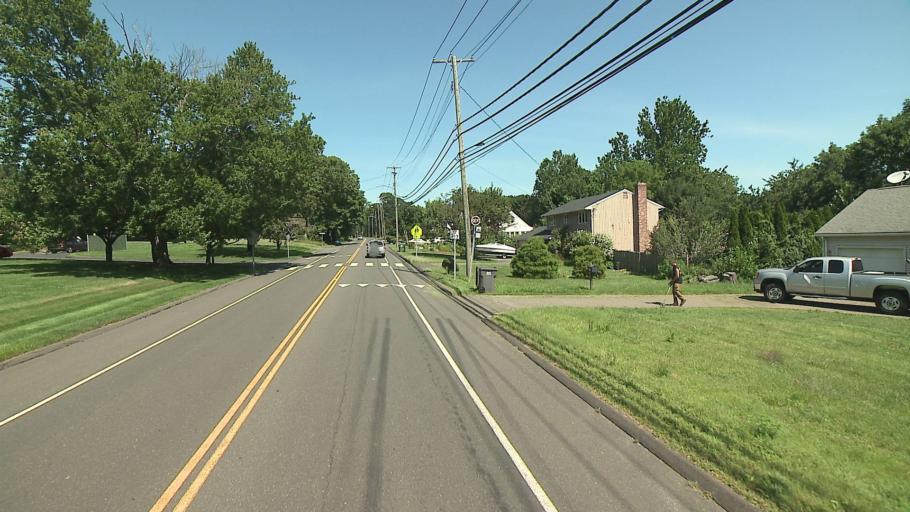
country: US
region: Connecticut
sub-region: Fairfield County
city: Trumbull
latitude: 41.2379
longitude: -73.2202
